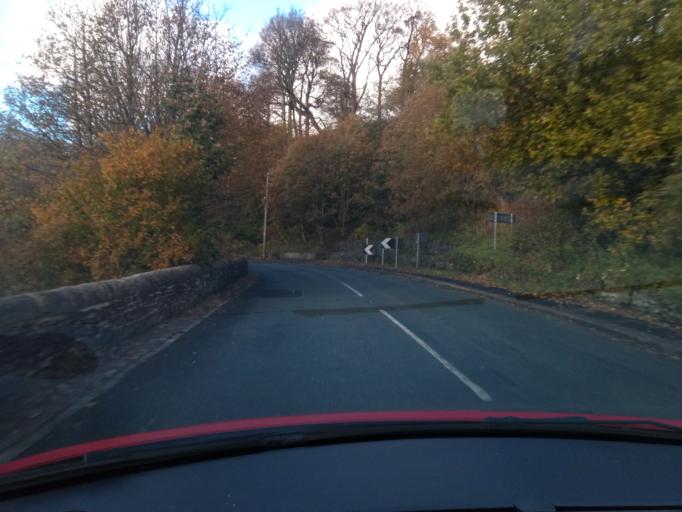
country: GB
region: England
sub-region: County Durham
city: Holwick
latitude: 54.7552
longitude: -2.2248
